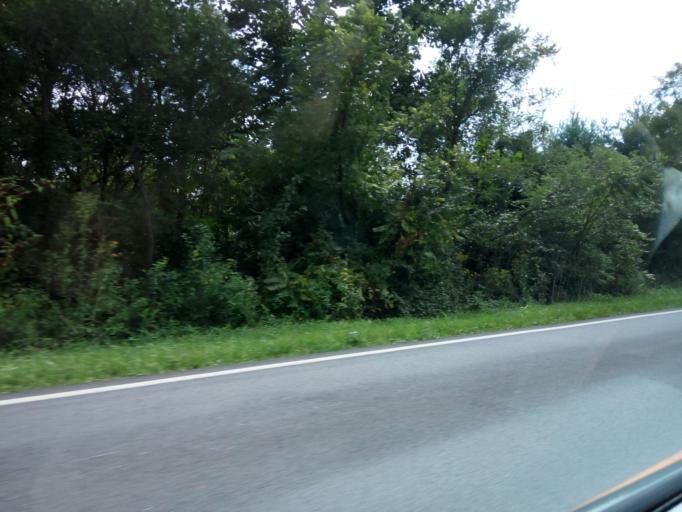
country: US
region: Kentucky
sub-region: Oldham County
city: Pewee Valley
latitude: 38.2797
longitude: -85.4871
